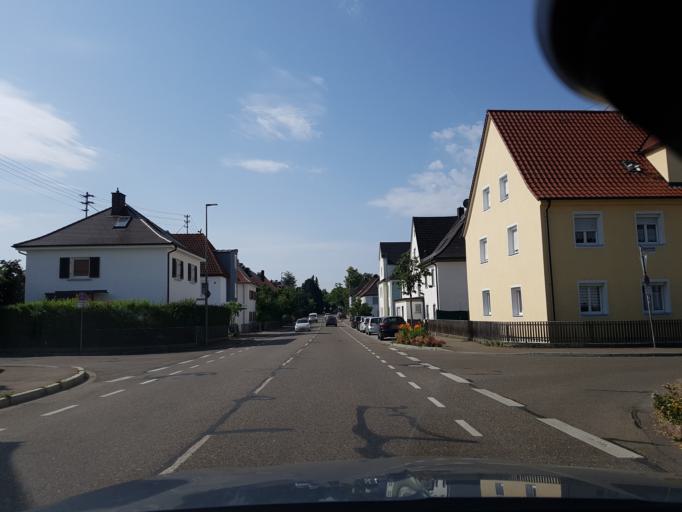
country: DE
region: Bavaria
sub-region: Swabia
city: Guenzburg
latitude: 48.4516
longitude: 10.2803
